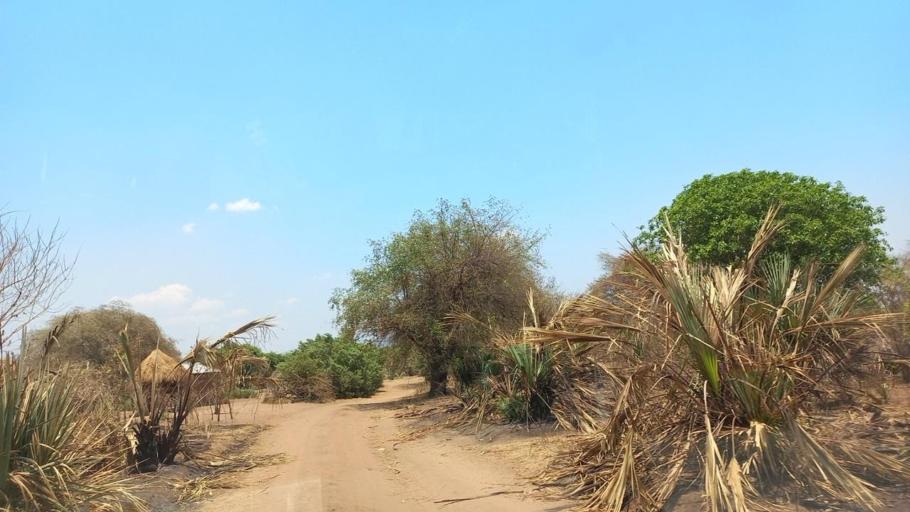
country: ZM
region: Lusaka
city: Luangwa
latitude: -15.1932
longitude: 30.1922
